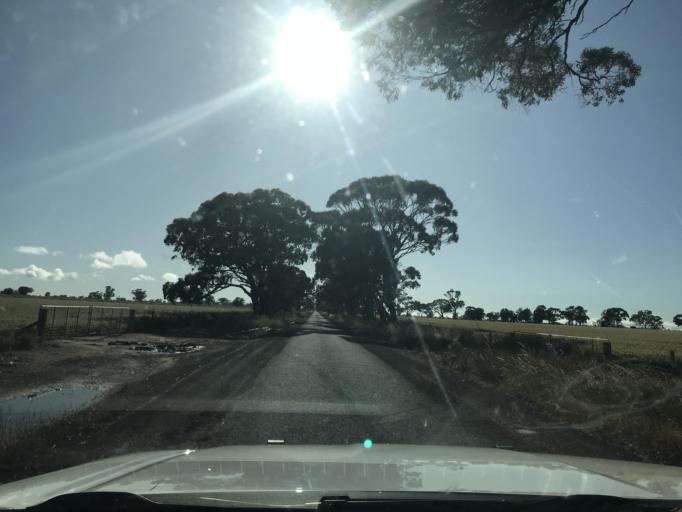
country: AU
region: Victoria
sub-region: Horsham
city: Horsham
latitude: -36.6920
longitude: 141.5434
